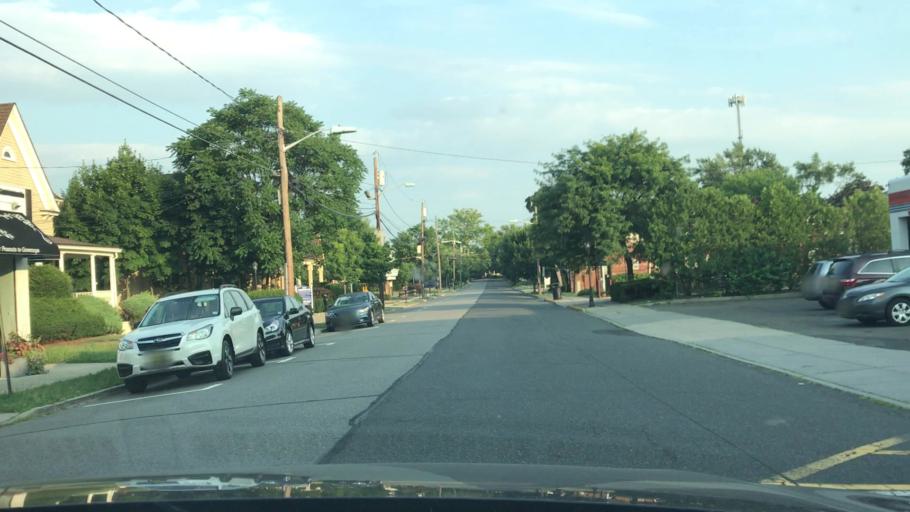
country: US
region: New Jersey
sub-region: Bergen County
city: Westwood
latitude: 40.9922
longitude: -74.0305
